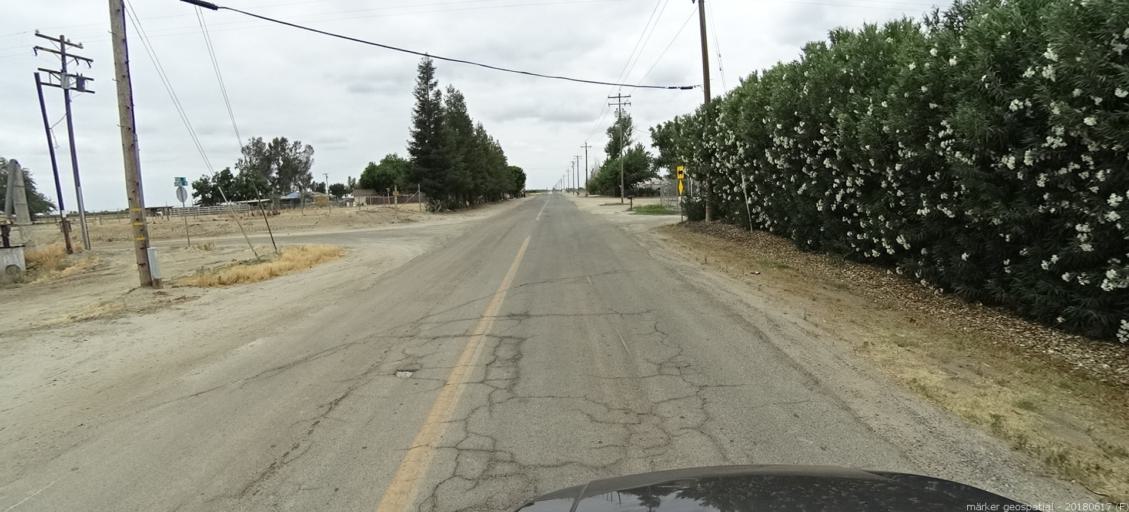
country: US
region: California
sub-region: Madera County
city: Madera
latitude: 36.8953
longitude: -120.1651
